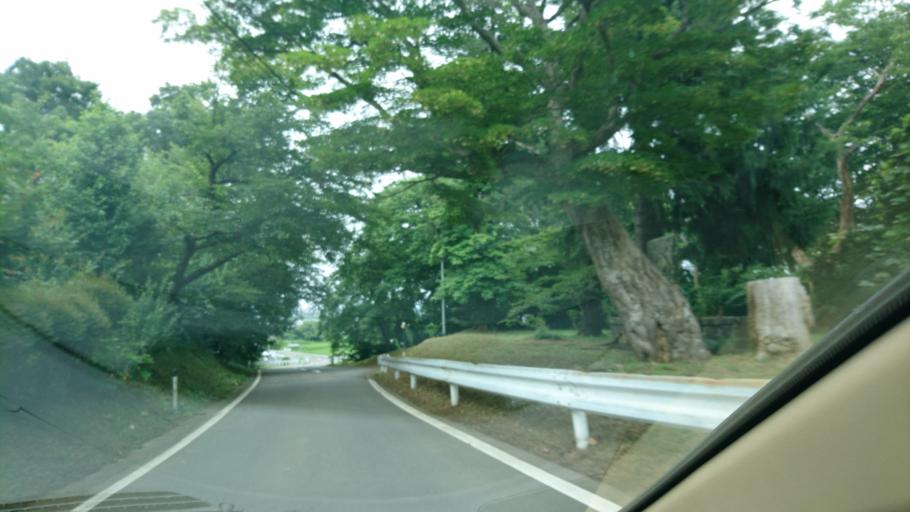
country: JP
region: Iwate
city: Kitakami
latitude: 39.2400
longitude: 141.1002
